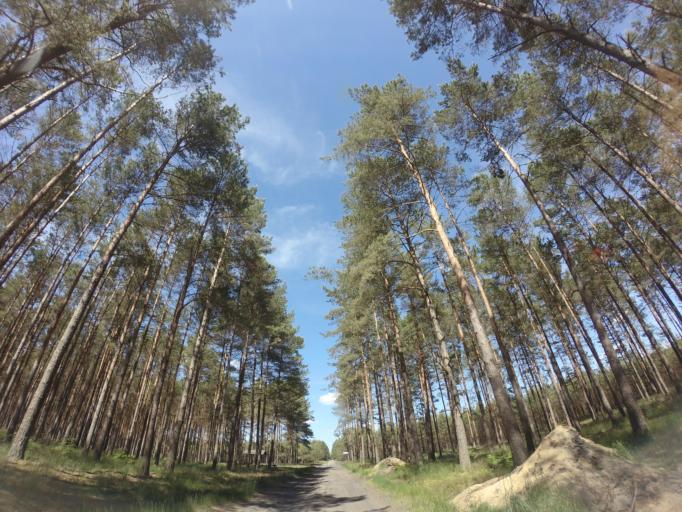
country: PL
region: West Pomeranian Voivodeship
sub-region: Powiat choszczenski
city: Drawno
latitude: 53.1548
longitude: 15.7856
